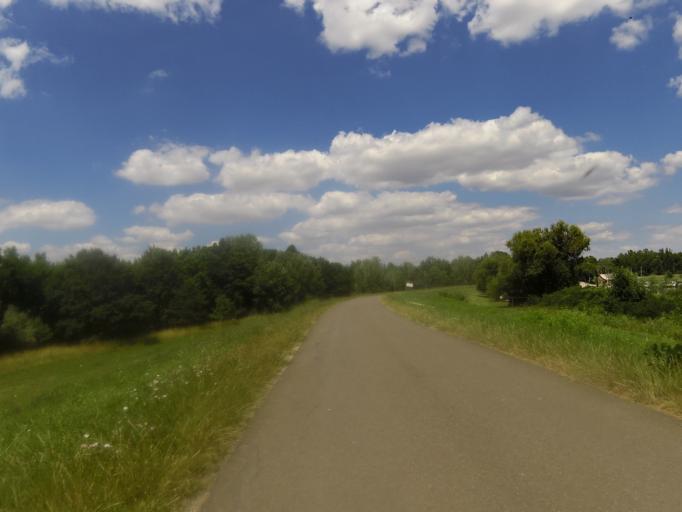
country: HU
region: Heves
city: Tiszanana
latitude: 47.5766
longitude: 20.6091
